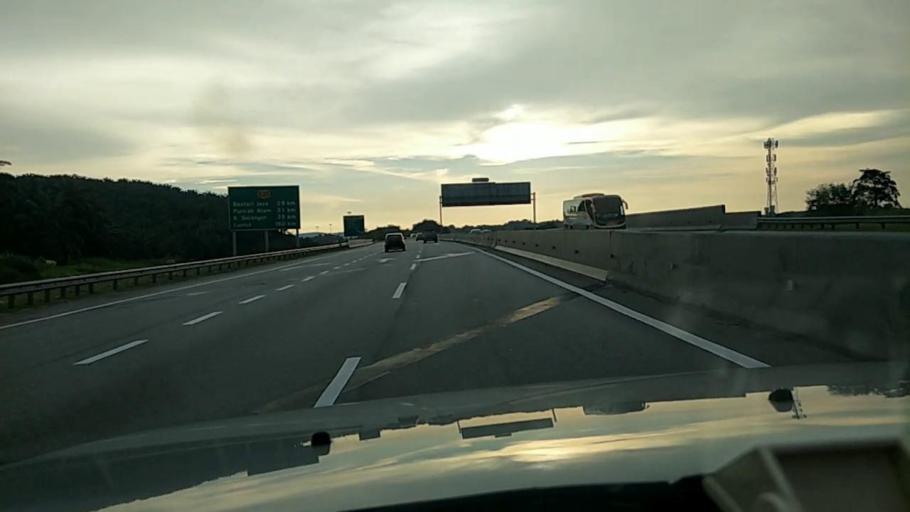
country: MY
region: Selangor
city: Kuang
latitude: 3.2714
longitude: 101.5400
